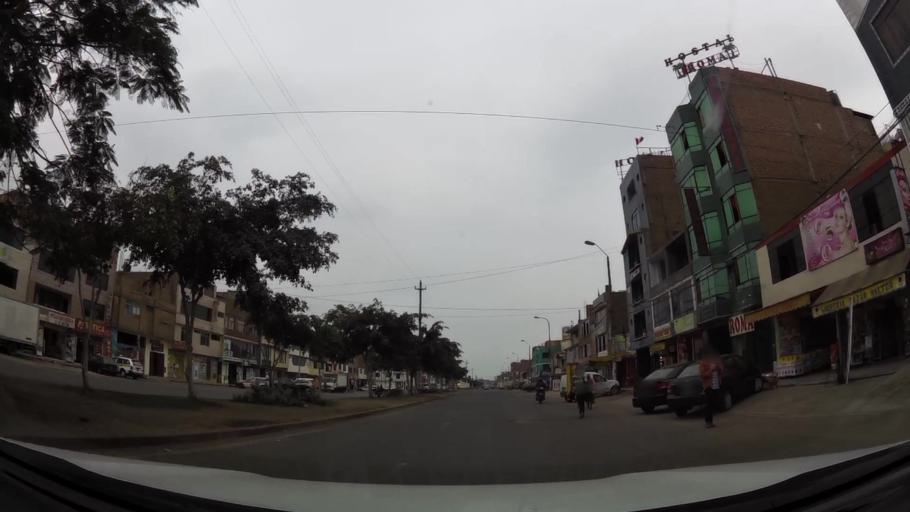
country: PE
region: Lima
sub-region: Lima
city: Independencia
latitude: -11.9776
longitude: -77.0837
